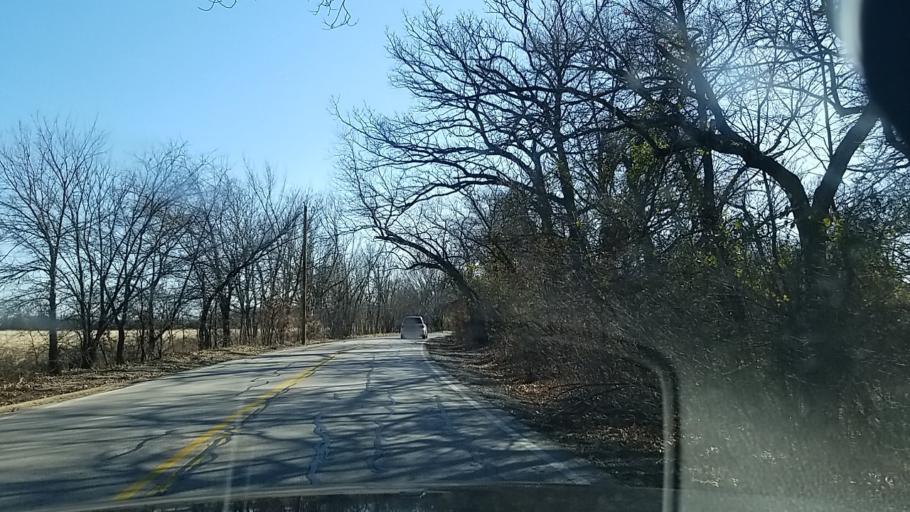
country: US
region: Texas
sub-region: Denton County
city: Argyle
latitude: 33.1511
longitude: -97.1406
